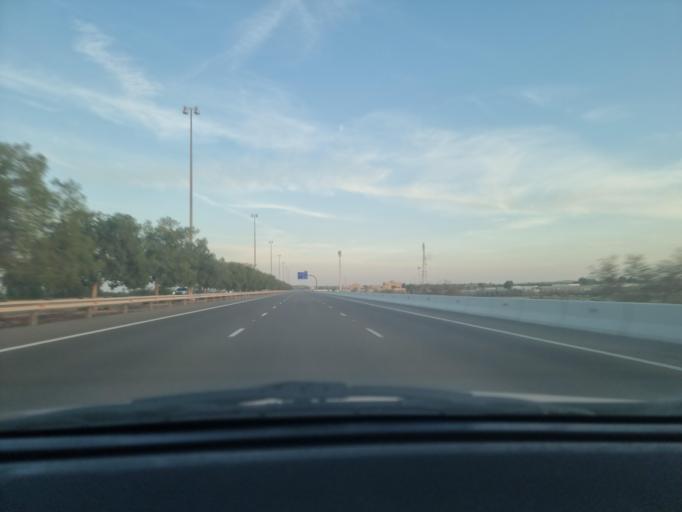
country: AE
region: Abu Dhabi
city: Al Ain
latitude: 24.1762
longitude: 55.0584
